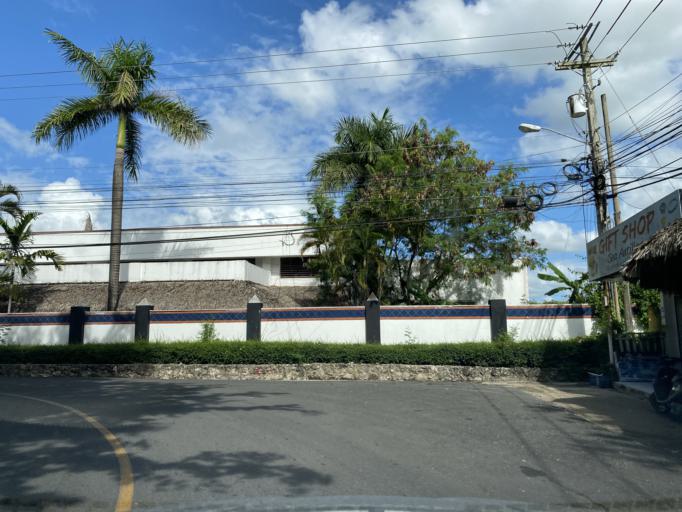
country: DO
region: Santo Domingo
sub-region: Santo Domingo
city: Boca Chica
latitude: 18.4493
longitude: -69.6033
